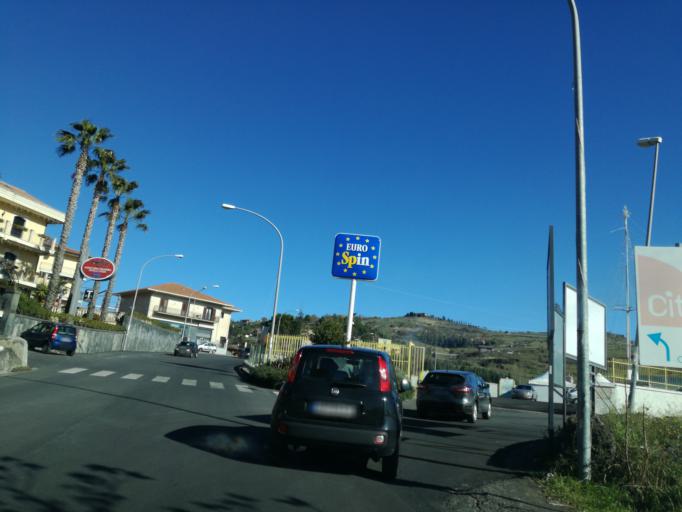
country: IT
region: Sicily
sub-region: Catania
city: Bronte
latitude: 37.7937
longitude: 14.8467
